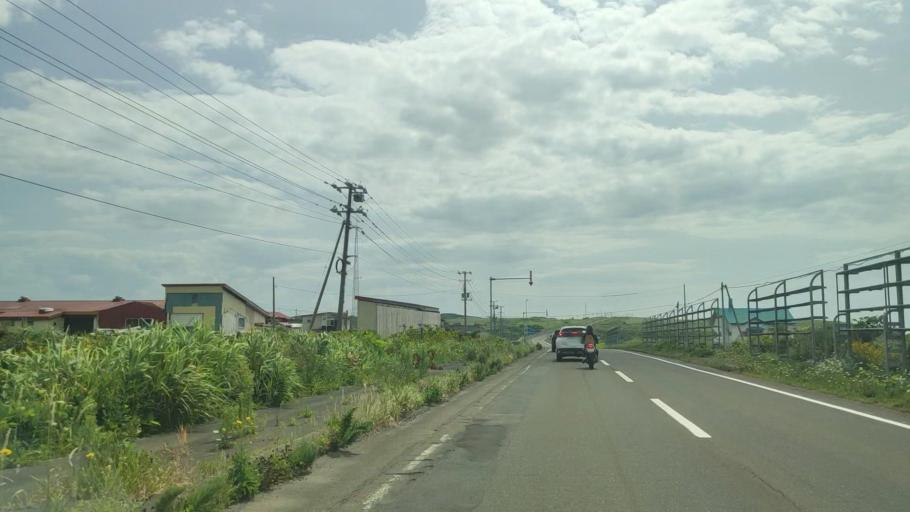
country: JP
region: Hokkaido
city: Rumoi
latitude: 44.4508
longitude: 141.7579
